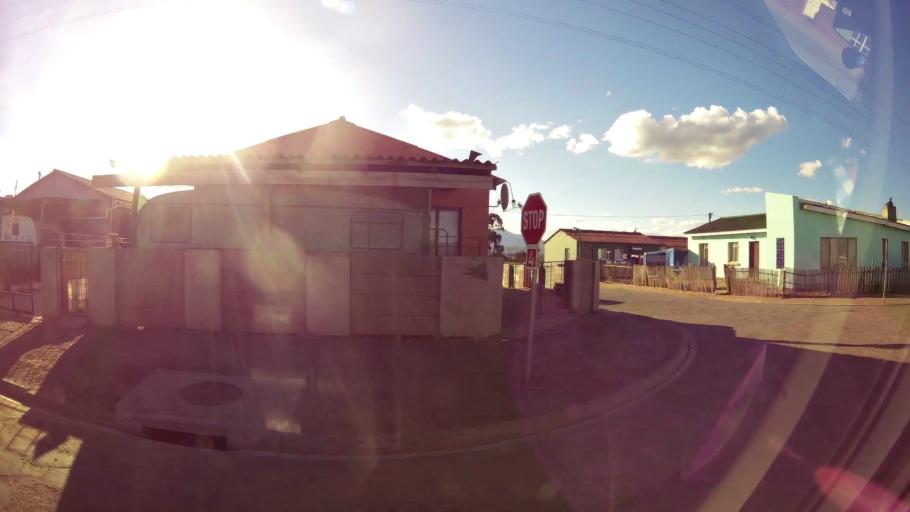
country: ZA
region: Western Cape
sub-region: Eden District Municipality
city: Riversdale
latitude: -34.1031
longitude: 20.9676
